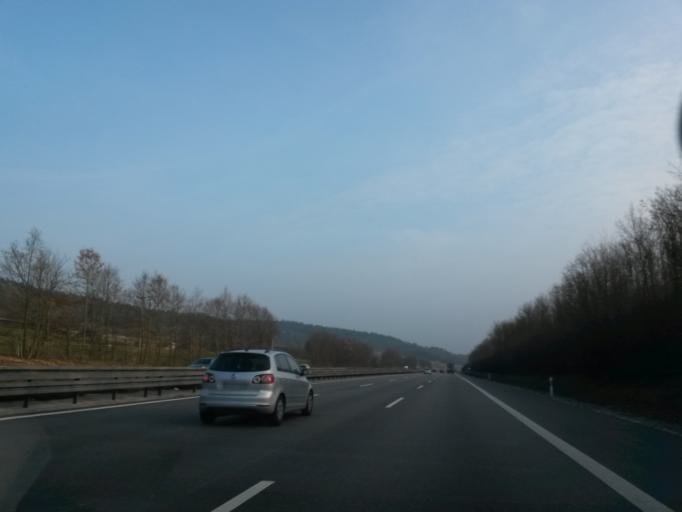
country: DE
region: Bavaria
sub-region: Regierungsbezirk Mittelfranken
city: Thalmassing
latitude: 49.1264
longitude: 11.2738
